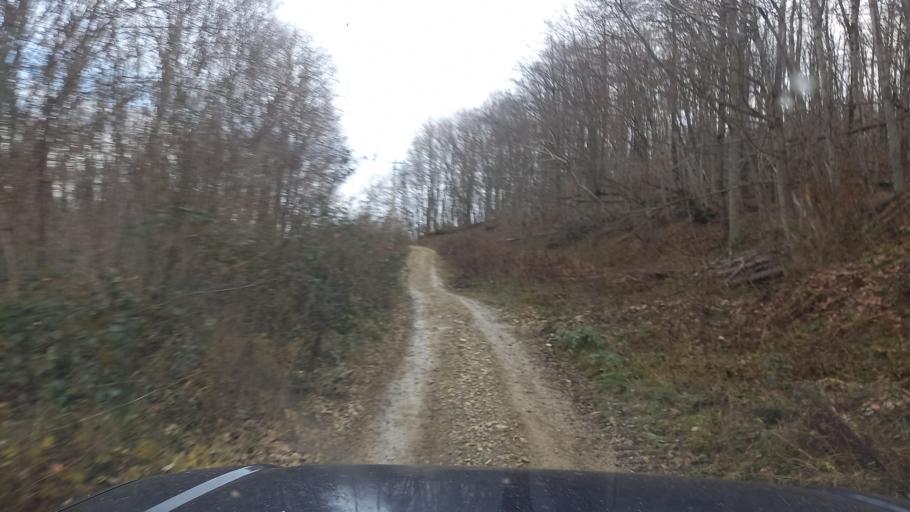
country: RU
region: Krasnodarskiy
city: Neftegorsk
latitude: 44.2172
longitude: 39.7208
